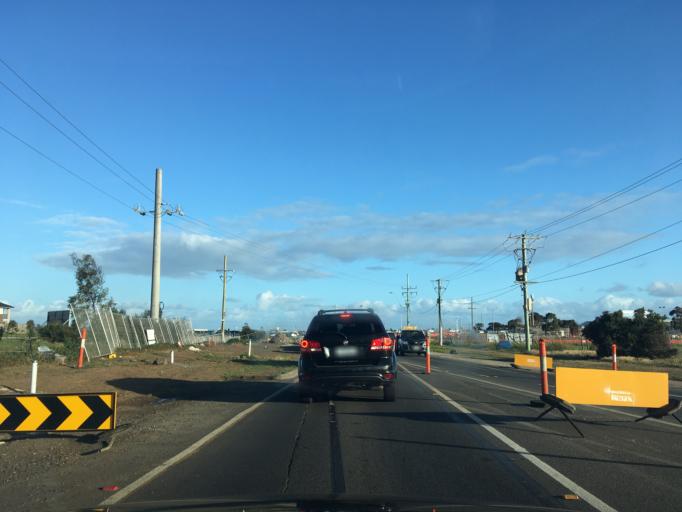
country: AU
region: Victoria
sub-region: Wyndham
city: Williams Landing
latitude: -37.8661
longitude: 144.7336
